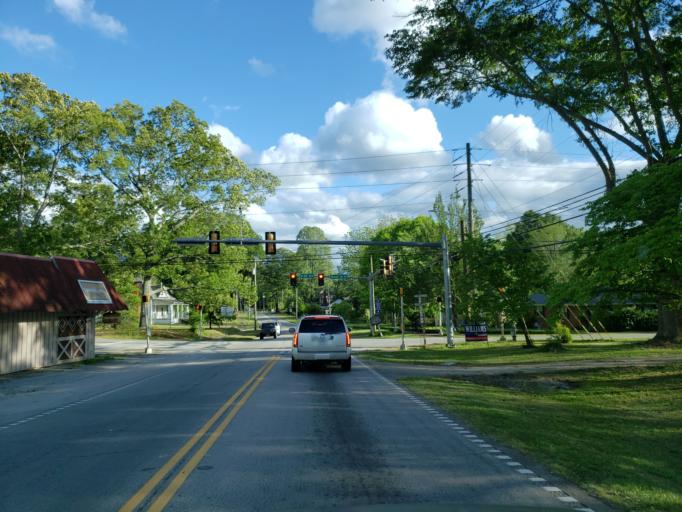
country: US
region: Georgia
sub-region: Haralson County
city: Tallapoosa
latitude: 33.7547
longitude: -85.2927
